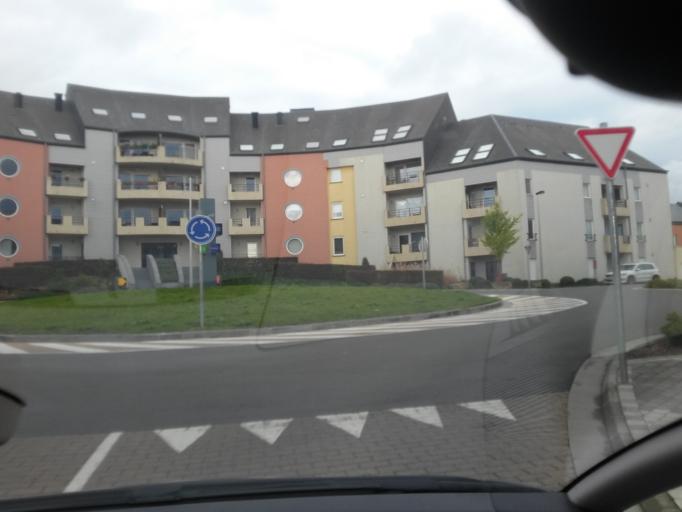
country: BE
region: Wallonia
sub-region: Province du Luxembourg
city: Arlon
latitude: 49.6929
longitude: 5.8086
